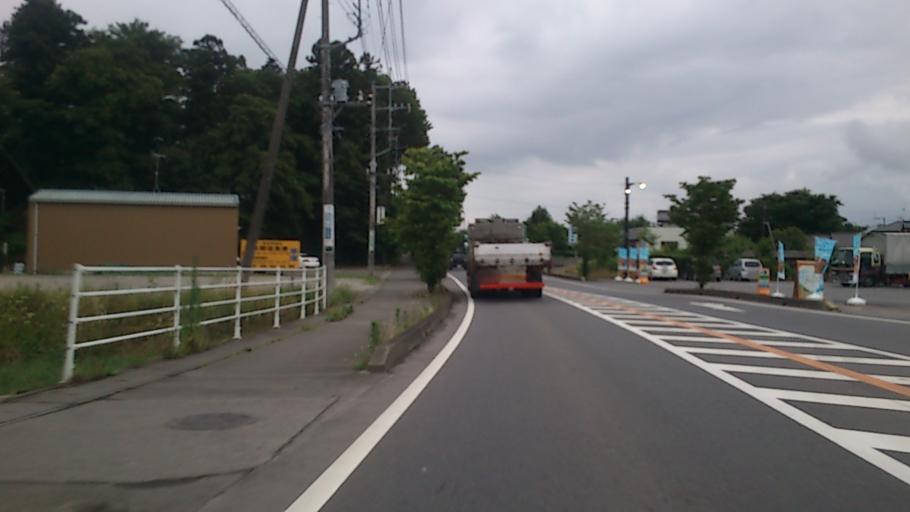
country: JP
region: Ibaraki
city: Iwai
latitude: 36.1056
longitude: 139.9002
